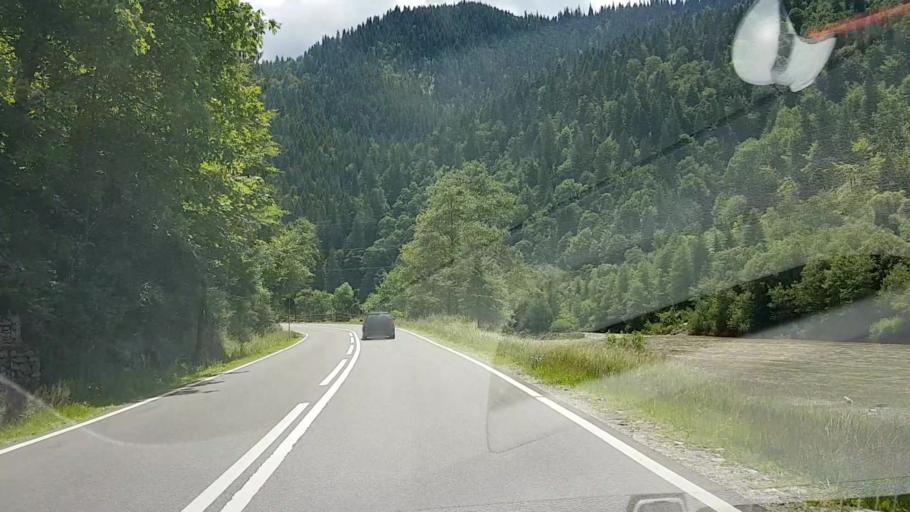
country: RO
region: Suceava
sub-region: Comuna Brosteni
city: Brosteni
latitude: 47.2600
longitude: 25.6689
